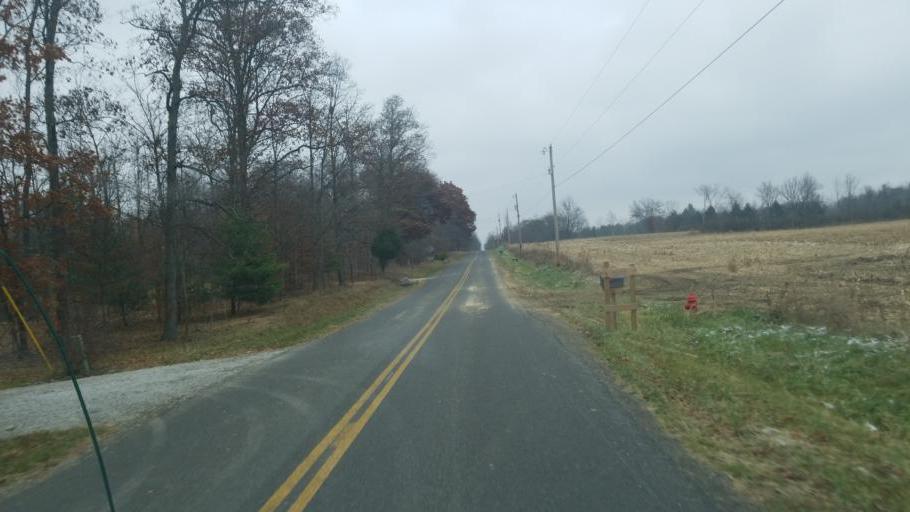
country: US
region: Ohio
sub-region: Medina County
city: Lodi
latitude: 41.1127
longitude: -82.0367
